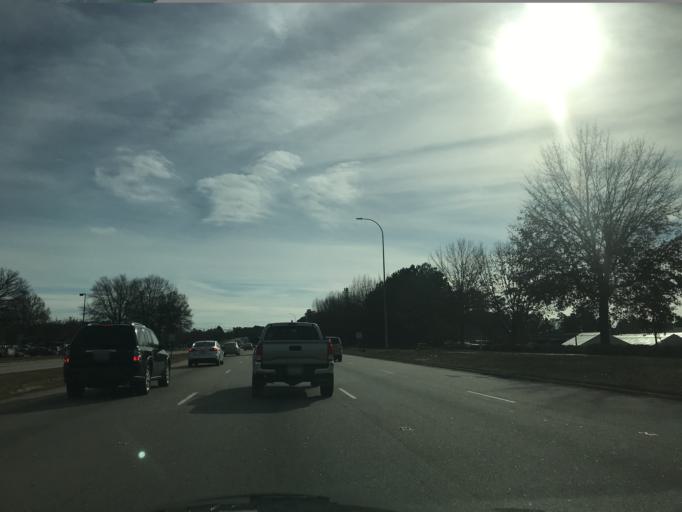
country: US
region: North Carolina
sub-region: Wake County
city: Raleigh
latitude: 35.8468
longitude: -78.5803
